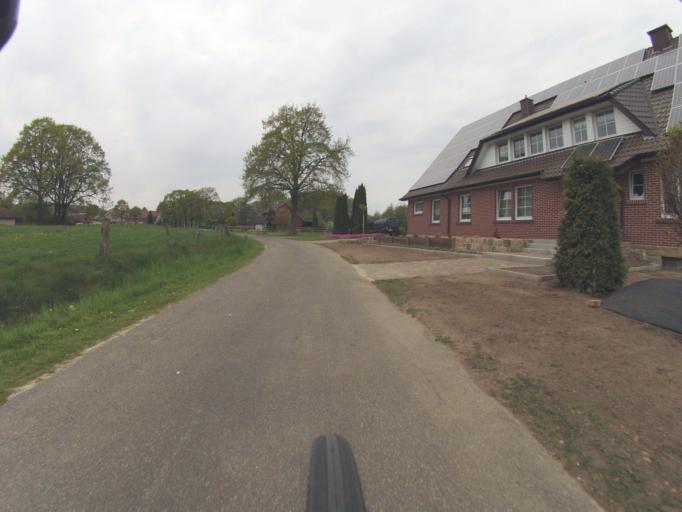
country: DE
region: North Rhine-Westphalia
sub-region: Regierungsbezirk Munster
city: Mettingen
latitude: 52.3105
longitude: 7.8073
